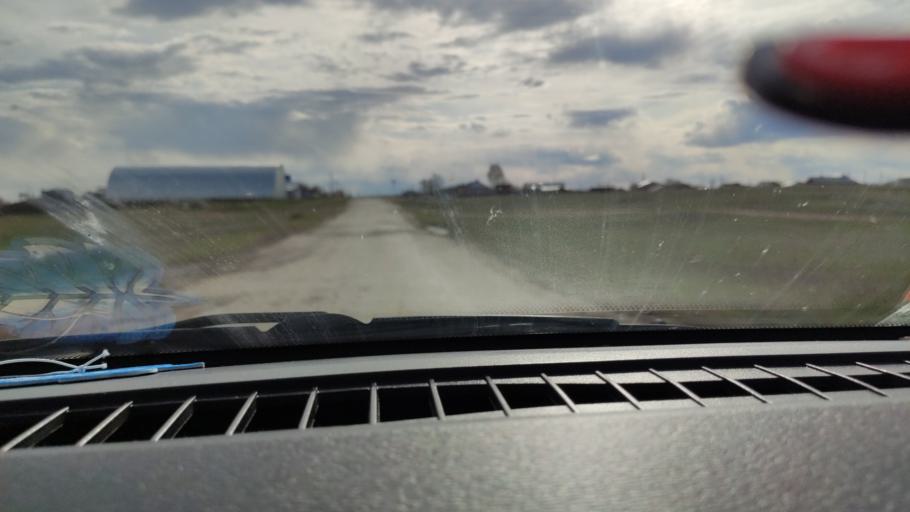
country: RU
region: Saratov
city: Rovnoye
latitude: 50.9318
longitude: 46.0901
